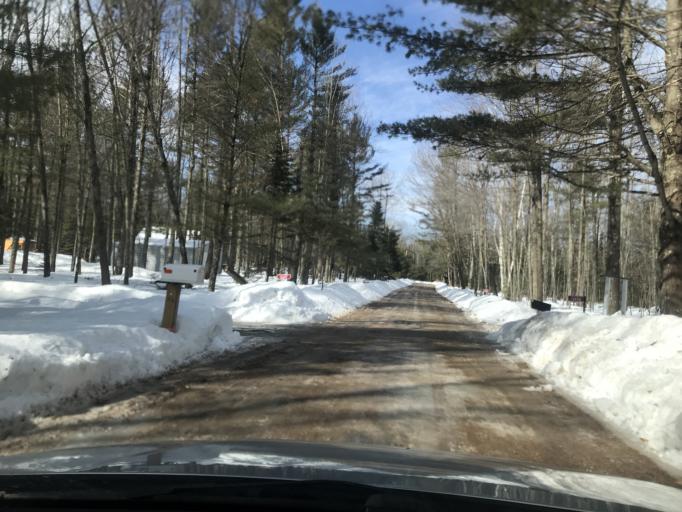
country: US
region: Wisconsin
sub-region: Menominee County
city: Legend Lake
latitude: 45.1198
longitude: -88.4434
